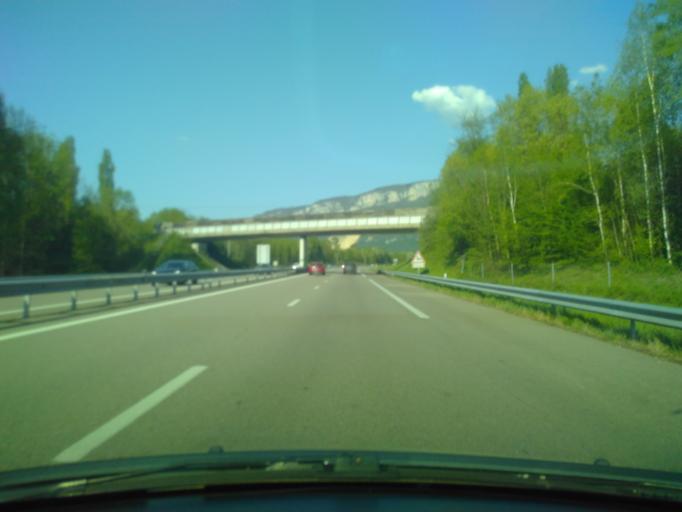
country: FR
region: Rhone-Alpes
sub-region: Departement de l'Isere
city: Veurey-Voroize
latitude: 45.3005
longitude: 5.5855
